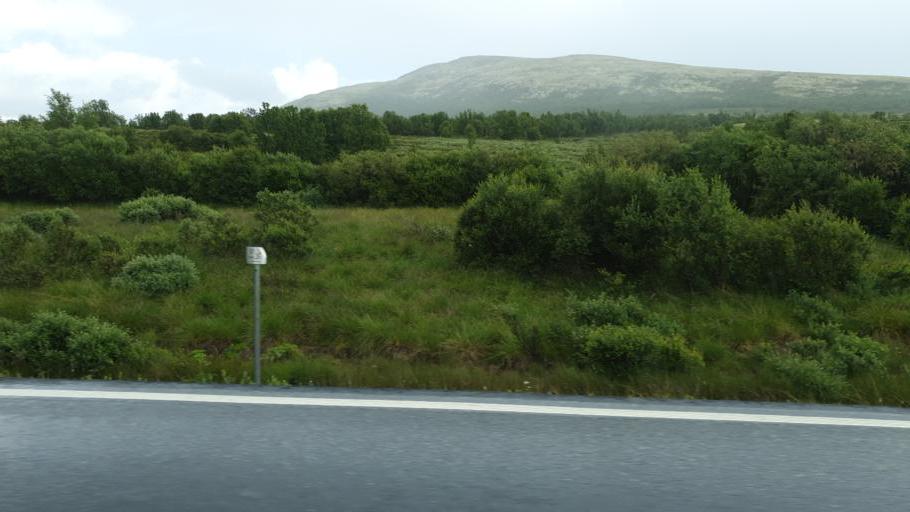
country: NO
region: Sor-Trondelag
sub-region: Oppdal
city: Oppdal
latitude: 62.2505
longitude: 9.5406
